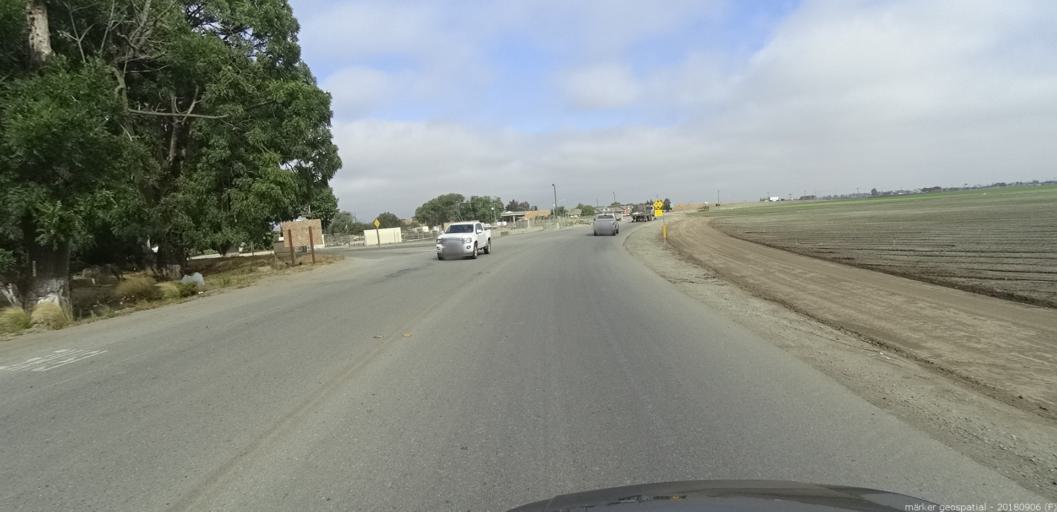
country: US
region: California
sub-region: Monterey County
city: Salinas
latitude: 36.6302
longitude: -121.6664
